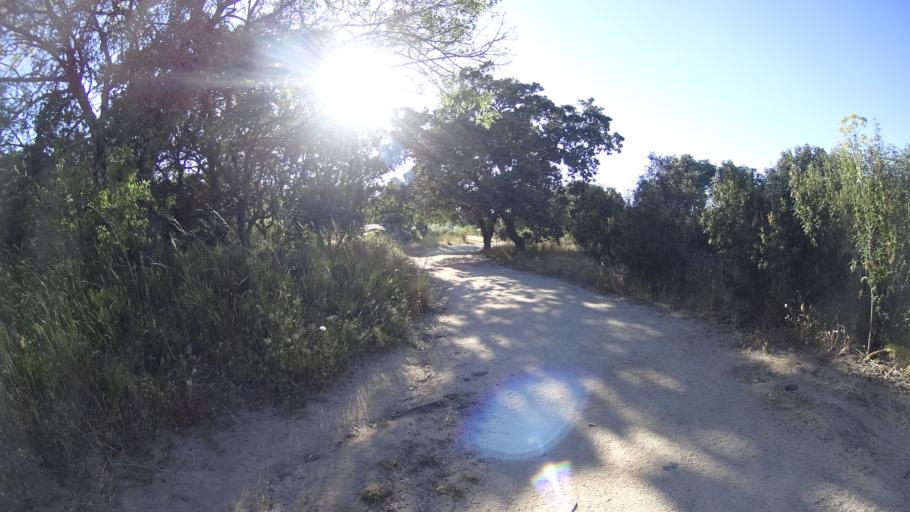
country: ES
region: Madrid
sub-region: Provincia de Madrid
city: Galapagar
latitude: 40.5902
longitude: -3.9750
